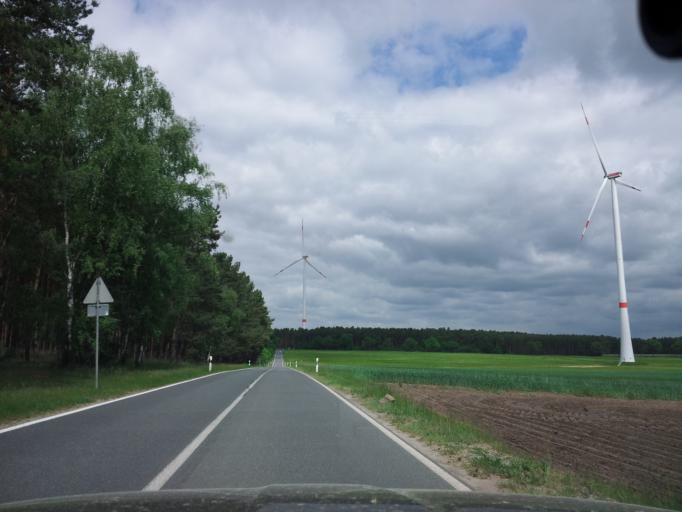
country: DE
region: Brandenburg
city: Linthe
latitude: 52.0898
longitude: 12.7958
